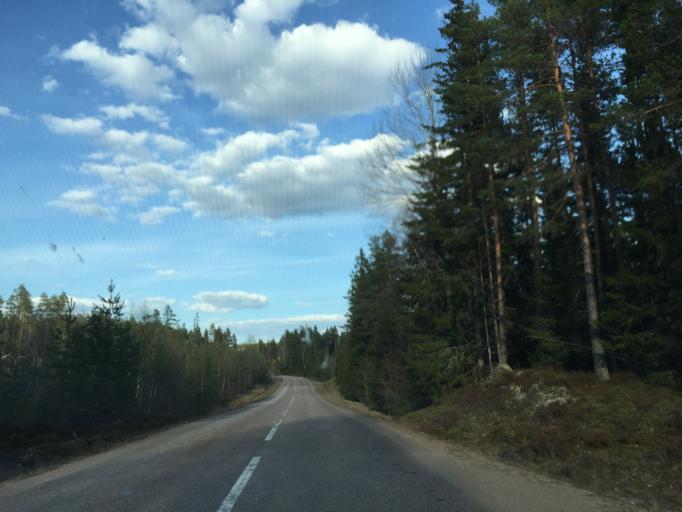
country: SE
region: Dalarna
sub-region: Vansbro Kommun
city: Jarna
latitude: 60.6030
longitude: 14.5143
